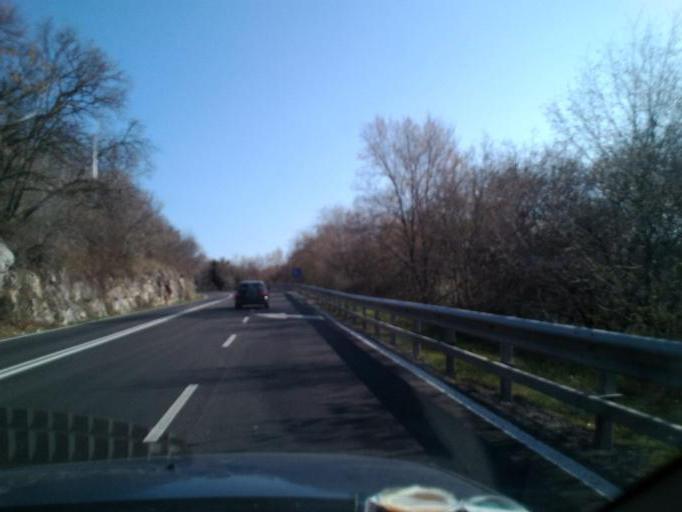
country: IT
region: Veneto
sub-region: Provincia di Verona
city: Grezzana
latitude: 45.5407
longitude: 11.0155
